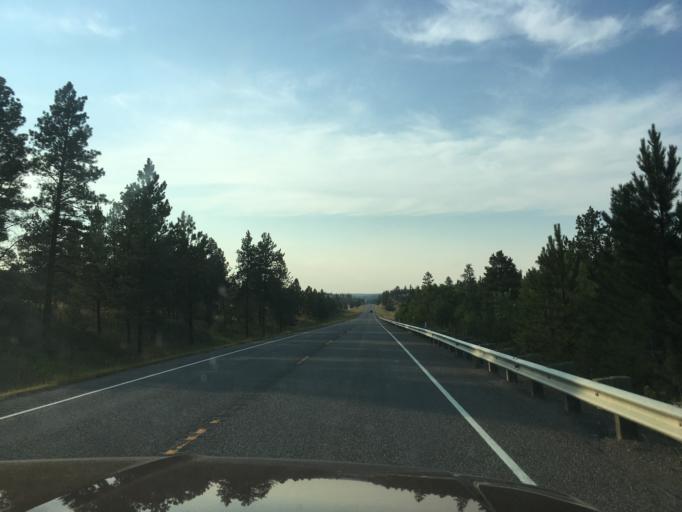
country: US
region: Montana
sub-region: Musselshell County
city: Roundup
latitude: 46.2655
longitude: -108.4685
